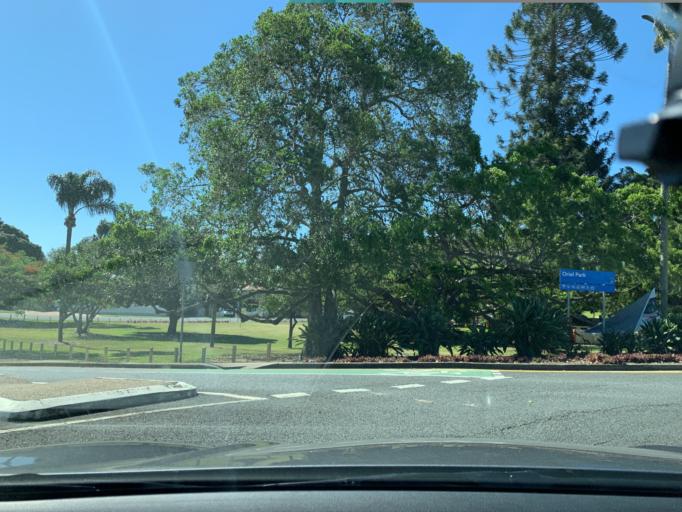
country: AU
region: Queensland
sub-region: Brisbane
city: Ascot
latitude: -27.4303
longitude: 153.0581
